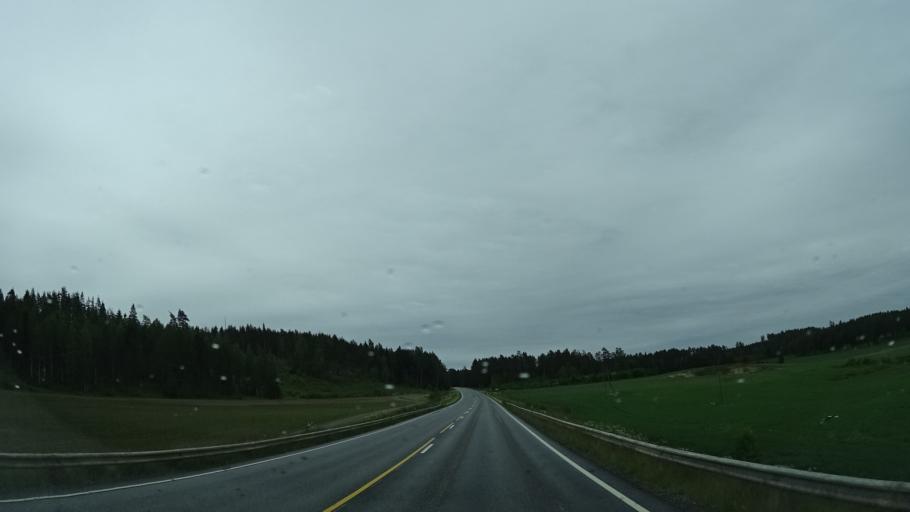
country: FI
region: Varsinais-Suomi
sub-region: Salo
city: Pernioe
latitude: 60.1716
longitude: 23.1516
